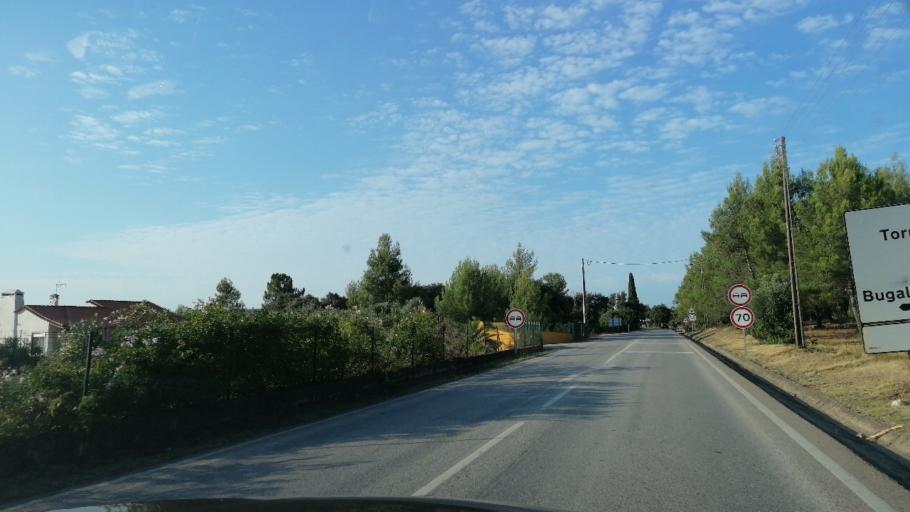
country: PT
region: Santarem
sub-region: Alcanena
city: Alcanena
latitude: 39.4283
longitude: -8.6335
